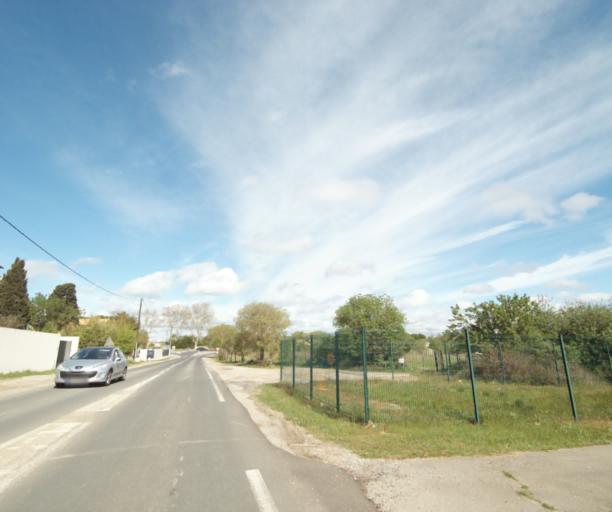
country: FR
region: Languedoc-Roussillon
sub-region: Departement de l'Herault
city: Villeneuve-les-Maguelone
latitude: 43.5535
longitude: 3.8457
